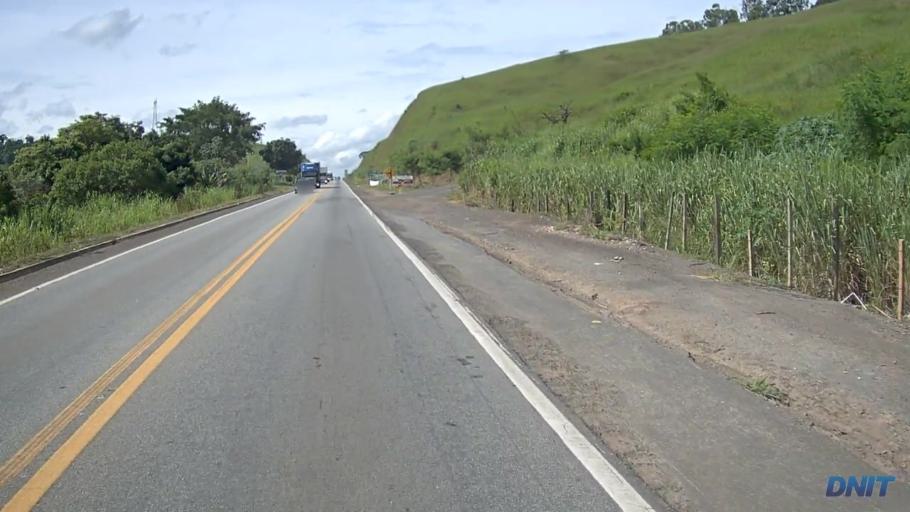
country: BR
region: Minas Gerais
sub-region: Ipatinga
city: Ipatinga
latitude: -19.4217
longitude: -42.4948
